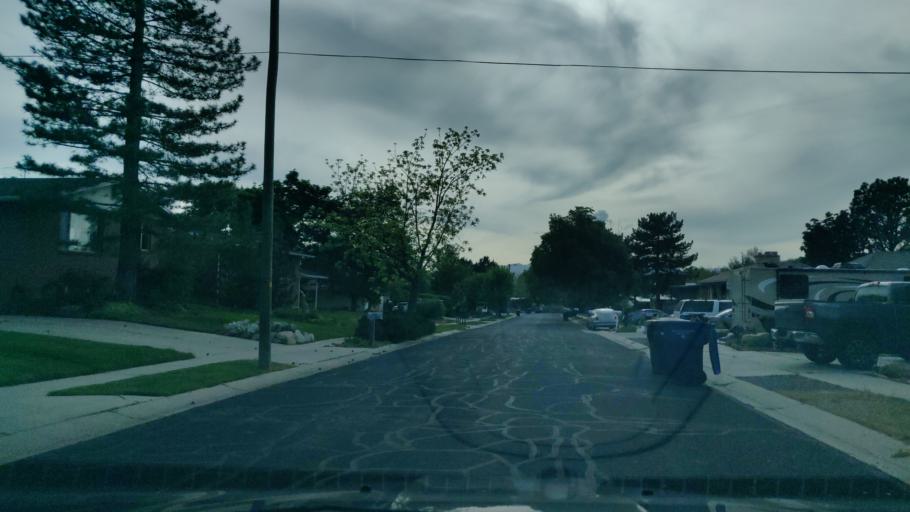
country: US
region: Utah
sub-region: Salt Lake County
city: Little Cottonwood Creek Valley
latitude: 40.6173
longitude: -111.8475
